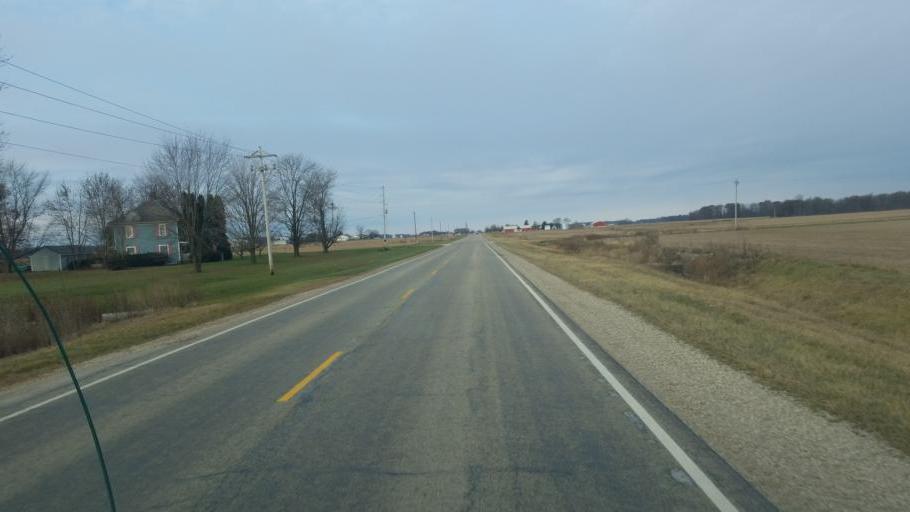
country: US
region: Ohio
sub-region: Mercer County
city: Fort Recovery
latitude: 40.5427
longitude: -84.8179
